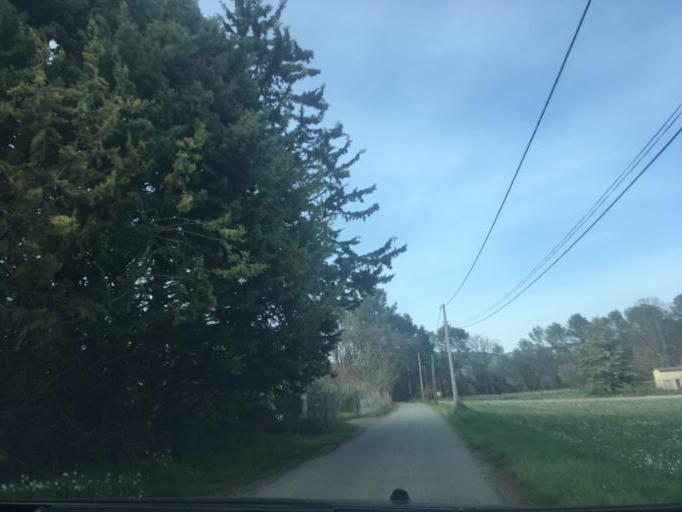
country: FR
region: Provence-Alpes-Cote d'Azur
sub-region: Departement du Var
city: Villecroze
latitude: 43.5652
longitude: 6.2843
